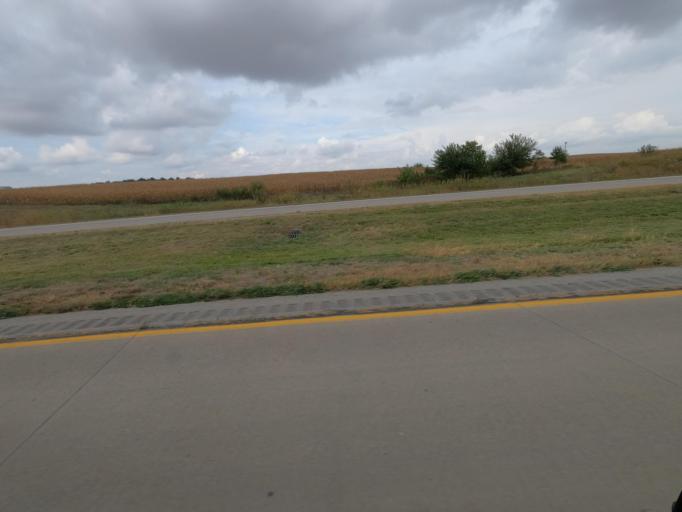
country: US
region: Iowa
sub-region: Jasper County
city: Prairie City
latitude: 41.5880
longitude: -93.2247
